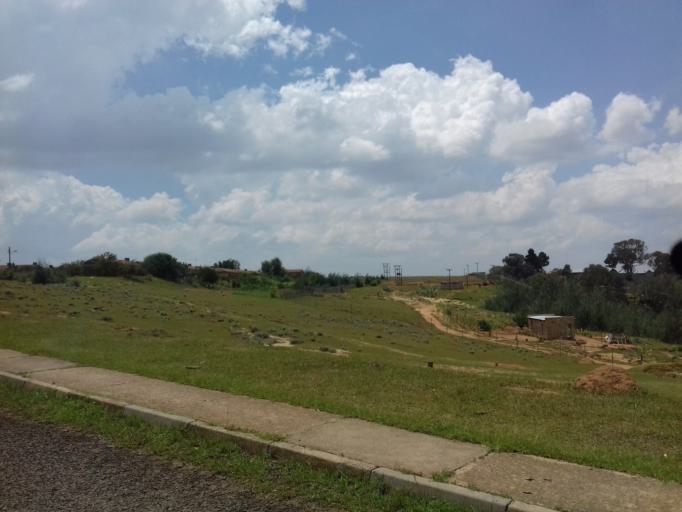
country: LS
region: Maseru
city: Maseru
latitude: -29.4545
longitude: 27.5626
